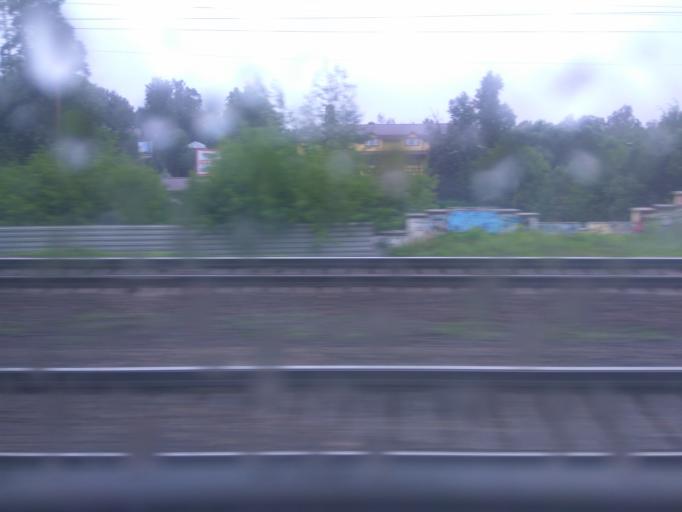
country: RU
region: Moskovskaya
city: Vidnoye
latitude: 55.5515
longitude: 37.6811
